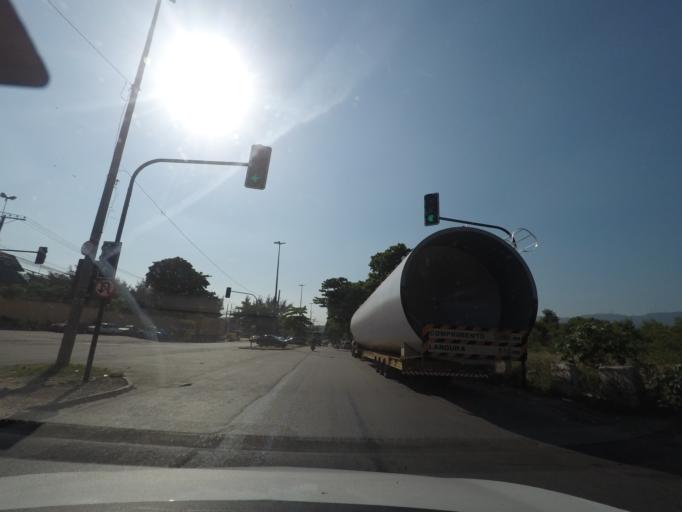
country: BR
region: Rio de Janeiro
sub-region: Rio De Janeiro
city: Rio de Janeiro
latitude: -22.8872
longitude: -43.2473
